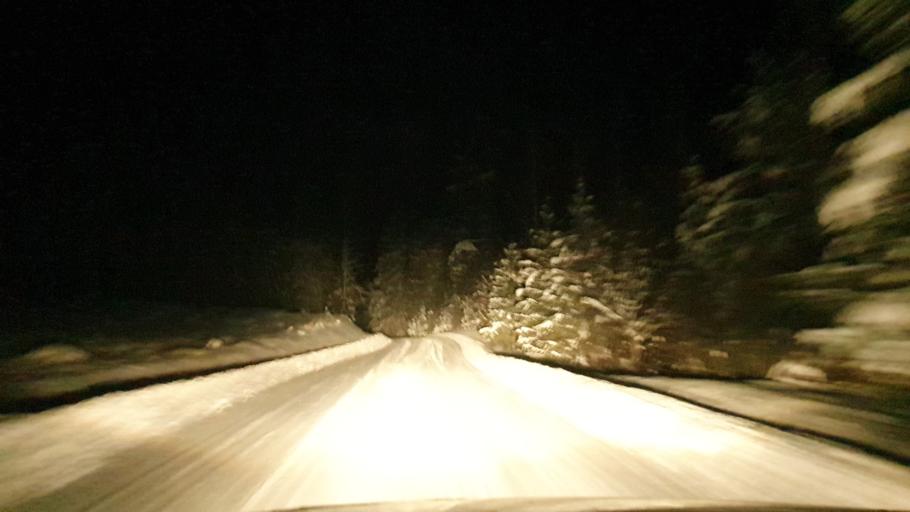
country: EE
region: Vorumaa
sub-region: Antsla vald
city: Vana-Antsla
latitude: 57.9637
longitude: 26.6188
